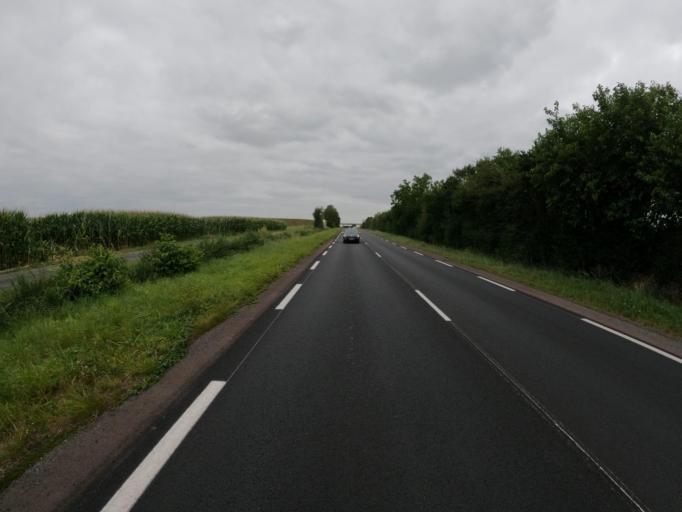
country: FR
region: Pays de la Loire
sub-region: Departement de la Vendee
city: Benet
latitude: 46.3955
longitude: -0.6504
